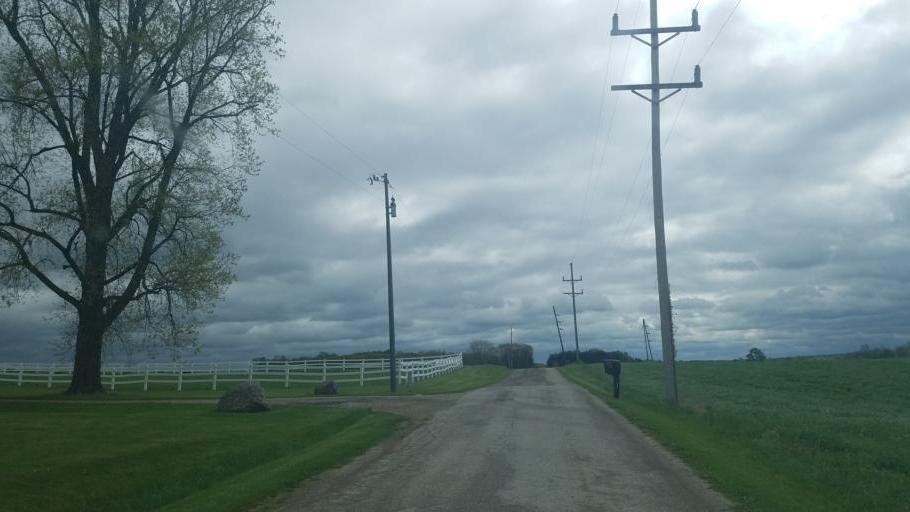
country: US
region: Ohio
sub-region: Knox County
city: Fredericktown
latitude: 40.5503
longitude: -82.5263
